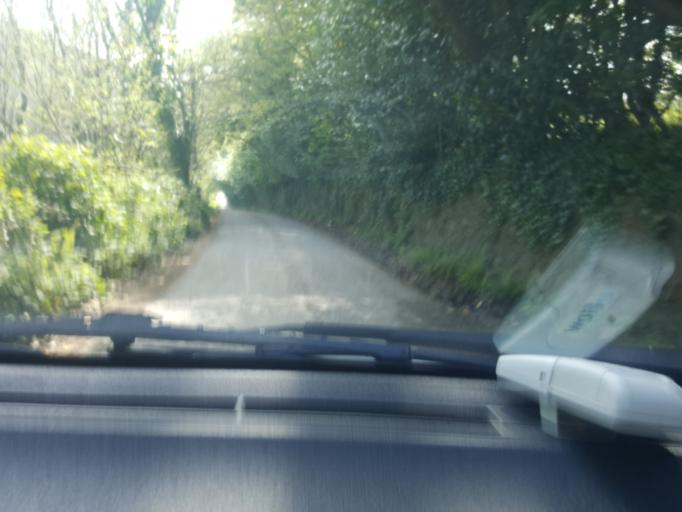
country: IE
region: Munster
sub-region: County Cork
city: Bandon
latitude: 51.7696
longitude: -8.6753
